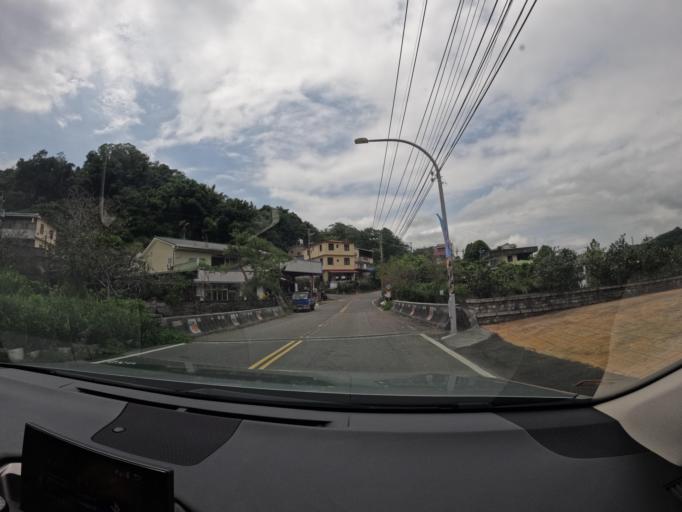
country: TW
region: Taiwan
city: Fengyuan
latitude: 24.3335
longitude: 120.8753
